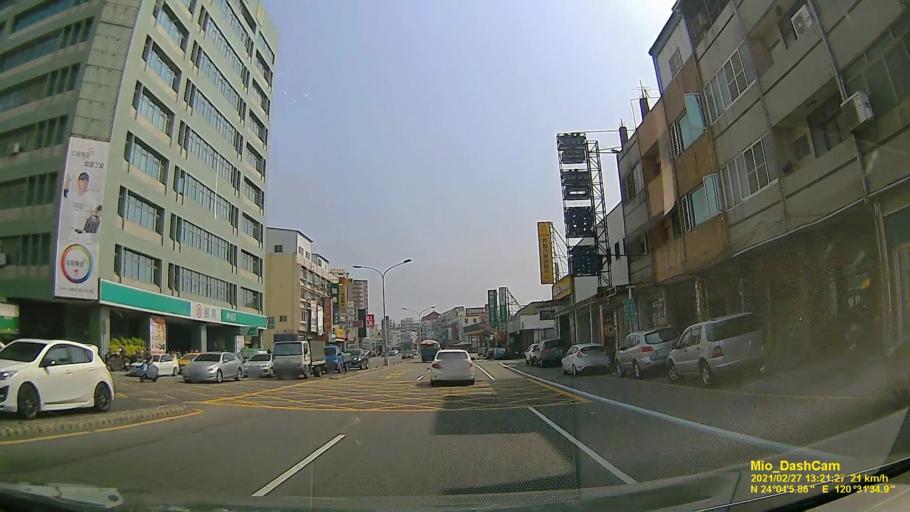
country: TW
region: Taiwan
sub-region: Changhua
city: Chang-hua
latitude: 24.0680
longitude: 120.5266
